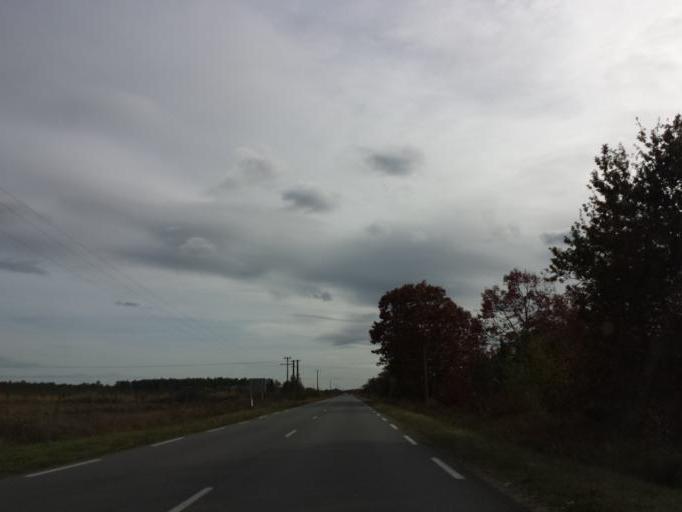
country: FR
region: Aquitaine
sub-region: Departement de la Gironde
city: Marcheprime
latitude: 44.7663
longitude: -0.9240
